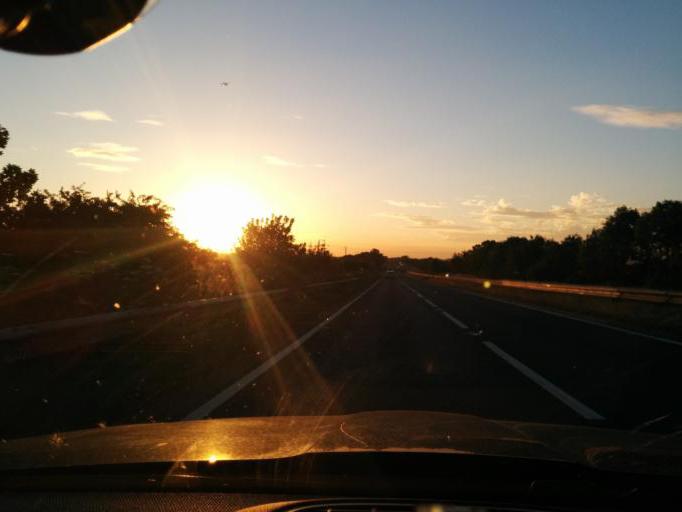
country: GB
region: England
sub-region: Northumberland
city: Seghill
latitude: 55.0518
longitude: -1.5566
